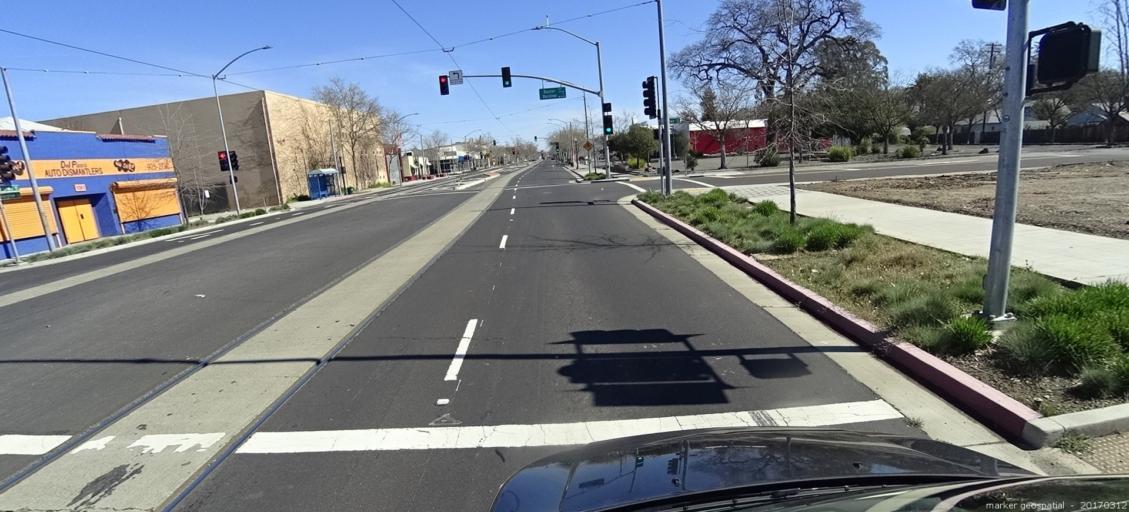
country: US
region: California
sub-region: Sacramento County
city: Sacramento
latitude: 38.6034
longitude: -121.4647
